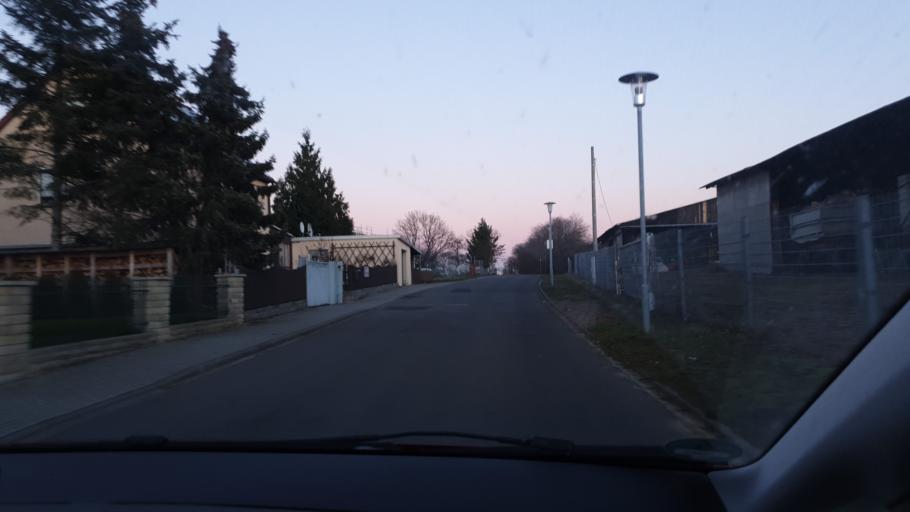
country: DE
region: Saxony
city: Mockrehna
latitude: 51.4716
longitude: 12.8104
